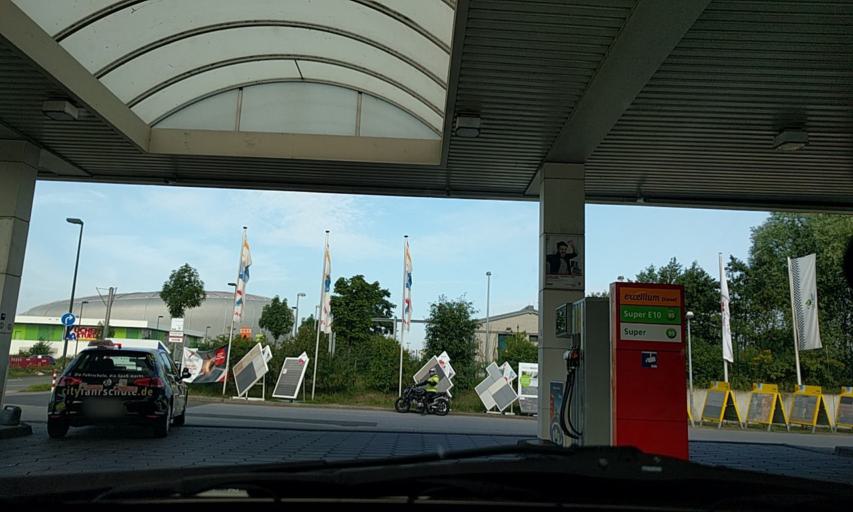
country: DE
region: North Rhine-Westphalia
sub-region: Regierungsbezirk Dusseldorf
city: Ratingen
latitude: 51.2718
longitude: 6.8164
